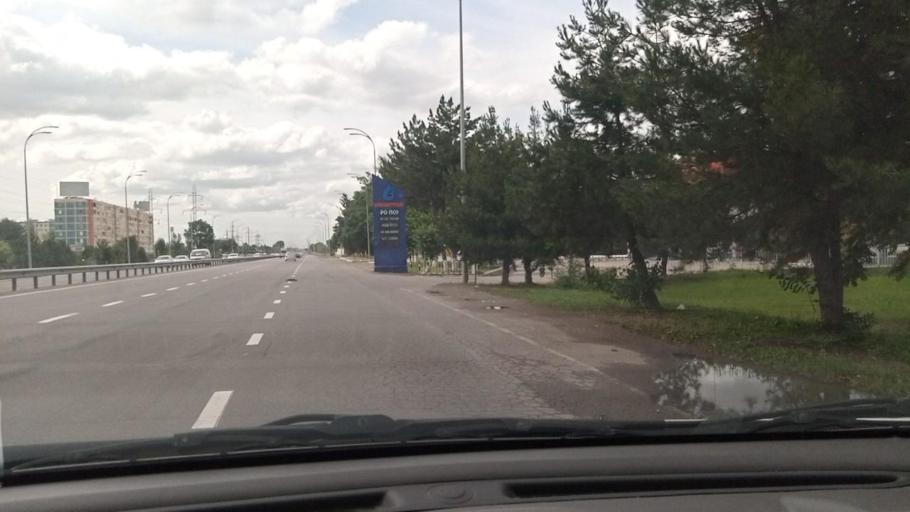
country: UZ
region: Toshkent Shahri
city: Bektemir
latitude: 41.2541
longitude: 69.3843
